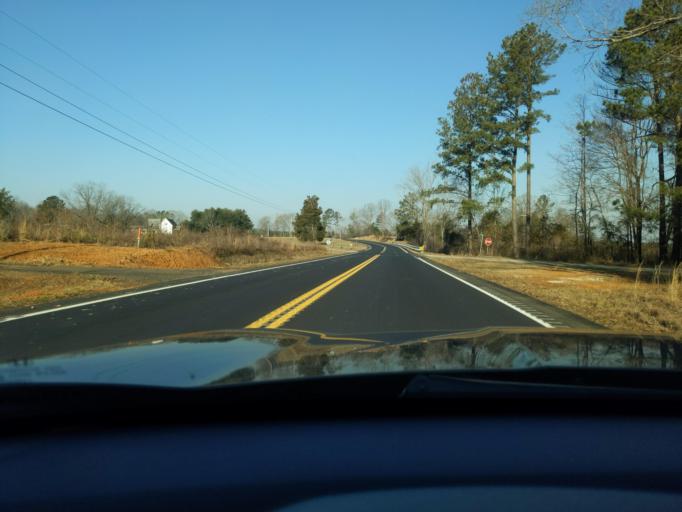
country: US
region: South Carolina
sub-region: Newberry County
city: Newberry
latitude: 34.2042
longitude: -81.8120
